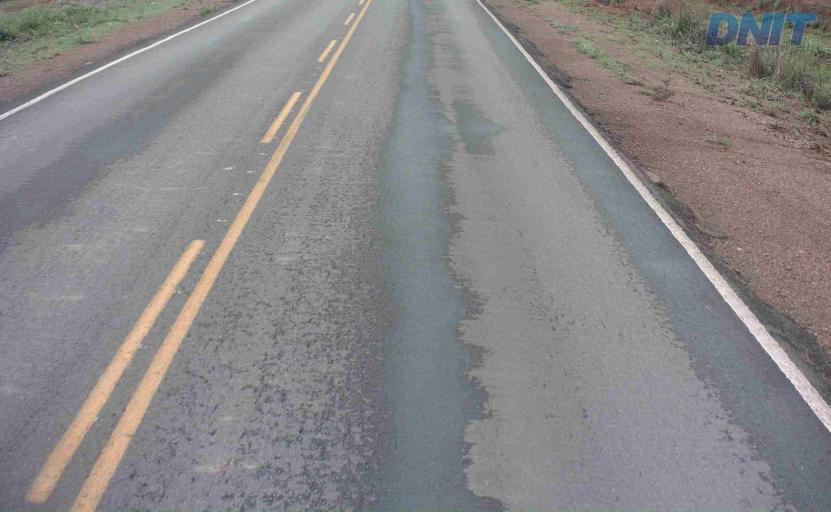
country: BR
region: Goias
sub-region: Padre Bernardo
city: Padre Bernardo
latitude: -15.2754
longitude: -48.2614
